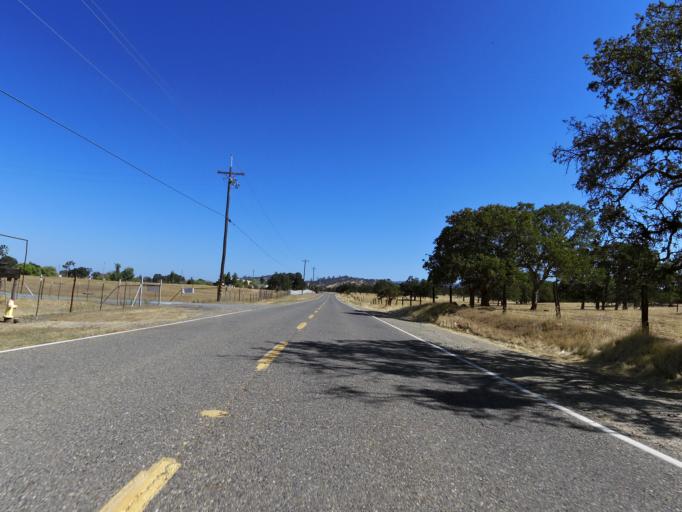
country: US
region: California
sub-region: Tuolumne County
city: Tuolumne City
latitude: 37.6491
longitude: -120.3113
